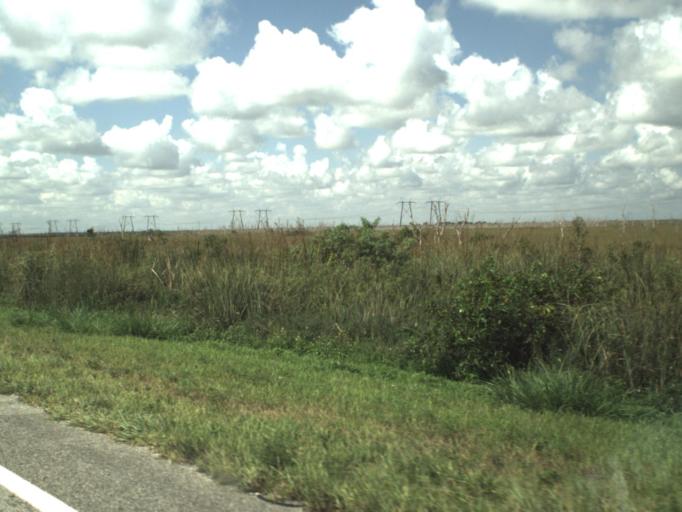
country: US
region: Florida
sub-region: Miami-Dade County
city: Palm Springs North
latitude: 25.9863
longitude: -80.4323
